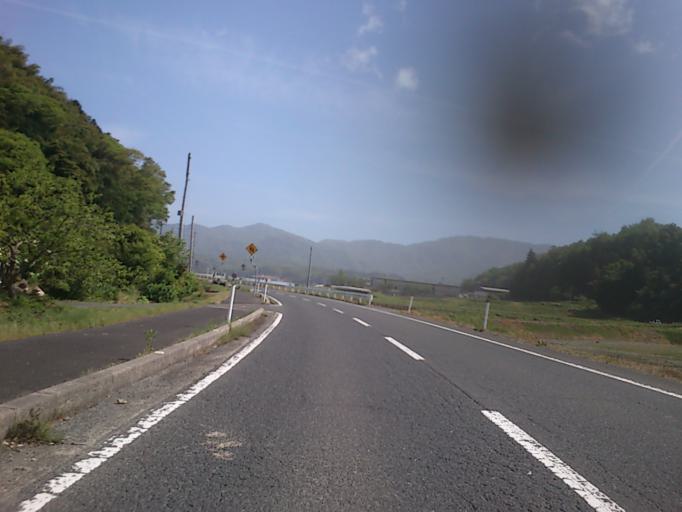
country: JP
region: Kyoto
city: Miyazu
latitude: 35.5840
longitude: 135.1313
